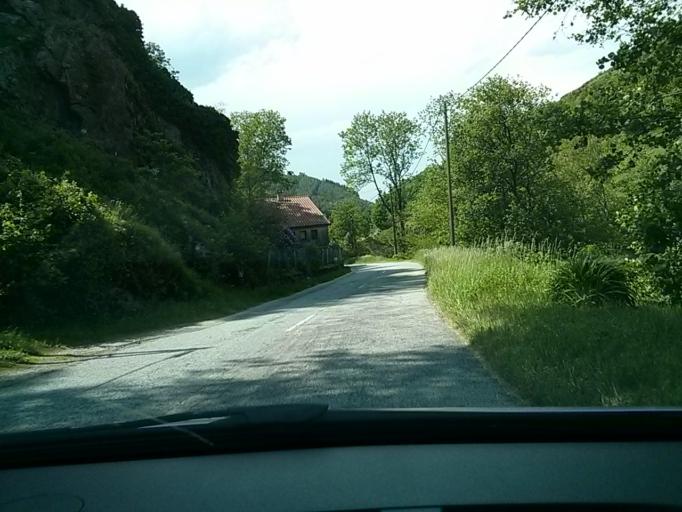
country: FR
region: Rhone-Alpes
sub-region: Departement de la Loire
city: Saint-Chamond
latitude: 45.4135
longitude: 4.5360
